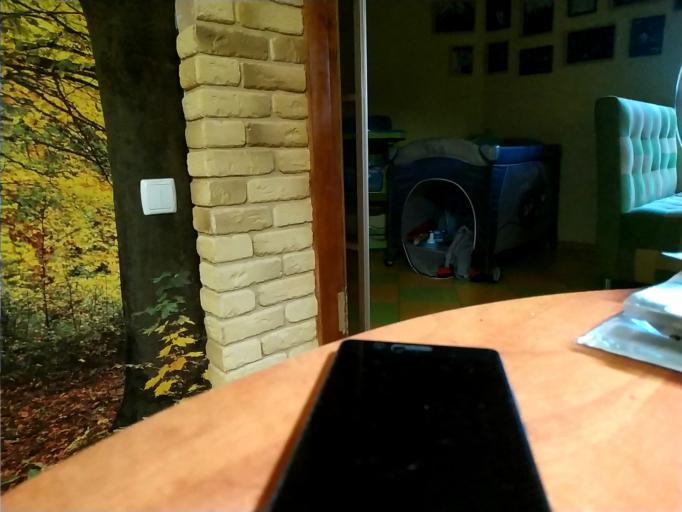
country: RU
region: Orjol
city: Znamenskoye
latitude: 53.4647
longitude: 35.5208
